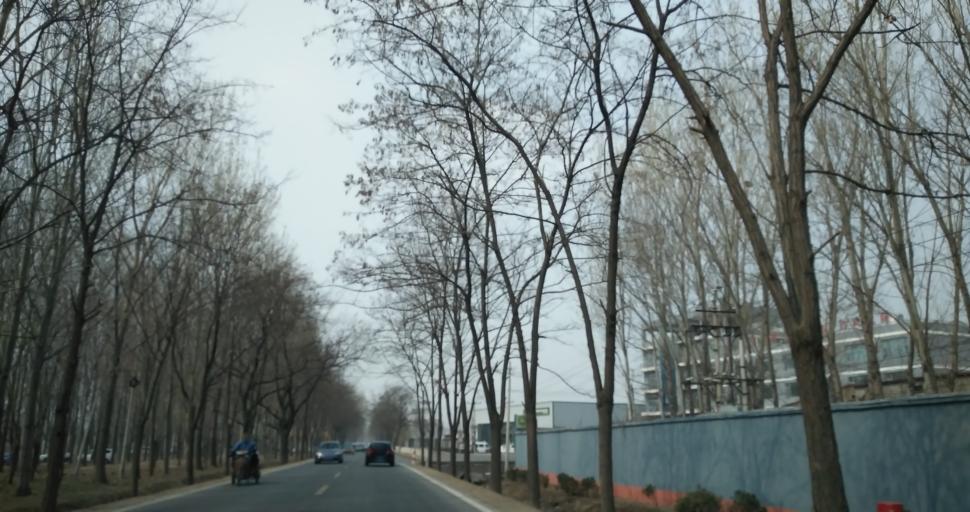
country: CN
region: Beijing
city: Qingyundian
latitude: 39.6889
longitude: 116.4988
